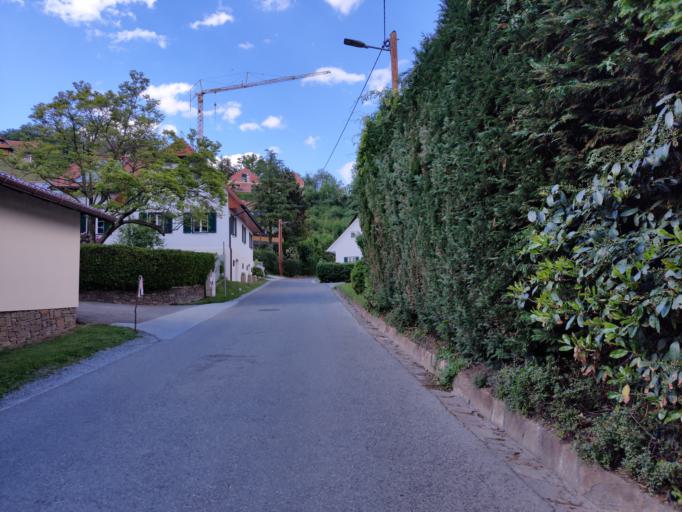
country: AT
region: Styria
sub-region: Graz Stadt
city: Wetzelsdorf
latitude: 47.0348
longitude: 15.3876
